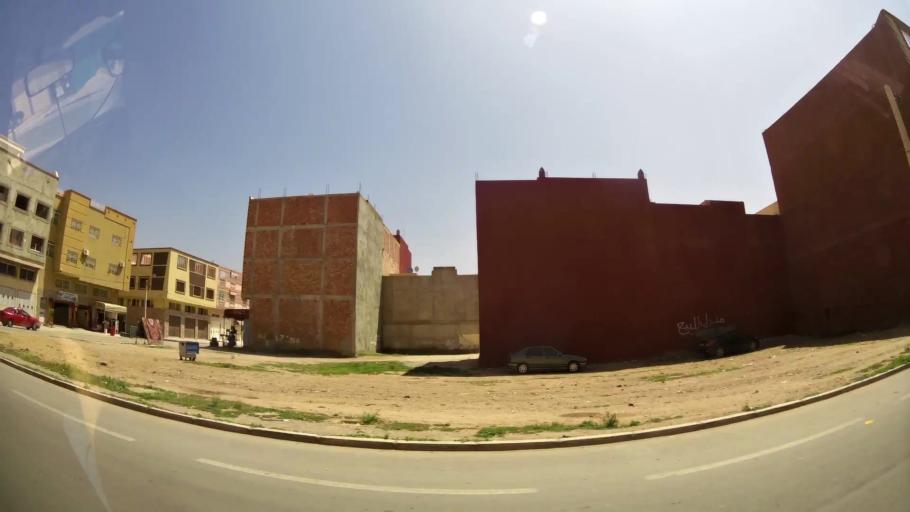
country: MA
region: Oriental
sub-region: Oujda-Angad
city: Oujda
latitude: 34.6963
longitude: -1.8854
